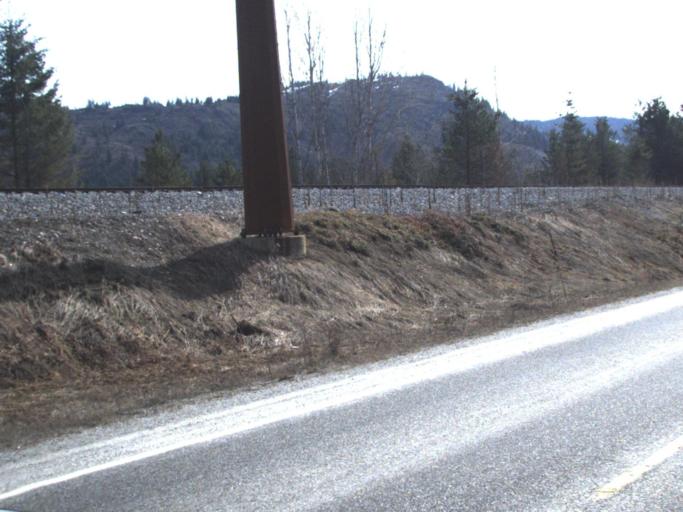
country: CA
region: British Columbia
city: Fruitvale
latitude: 48.6535
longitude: -117.3843
